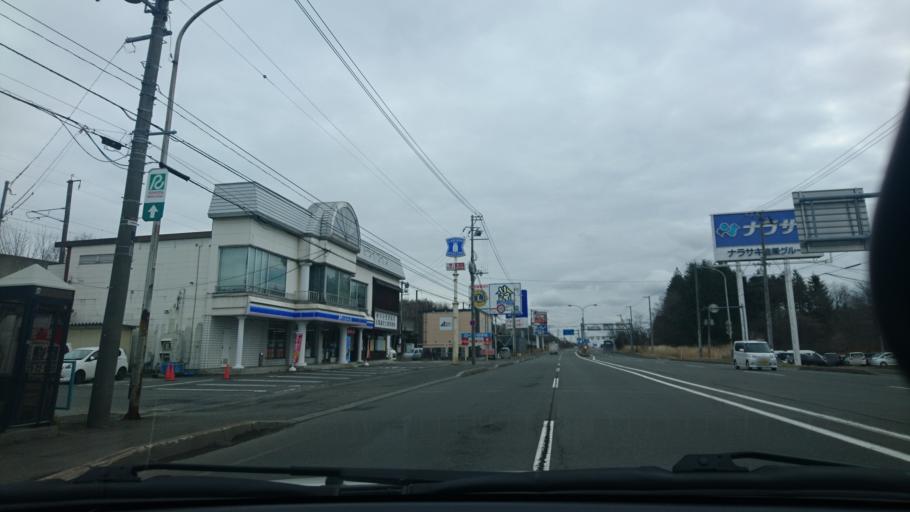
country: JP
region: Hokkaido
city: Chitose
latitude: 42.8210
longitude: 141.6594
